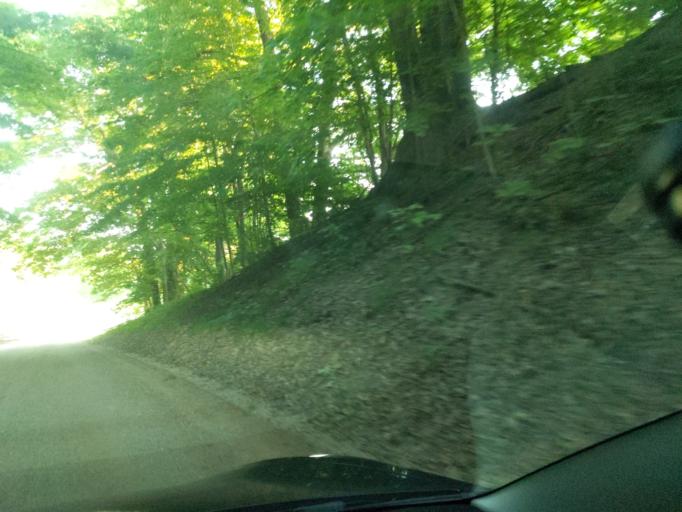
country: US
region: Michigan
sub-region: Barry County
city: Nashville
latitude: 42.5325
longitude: -85.1134
